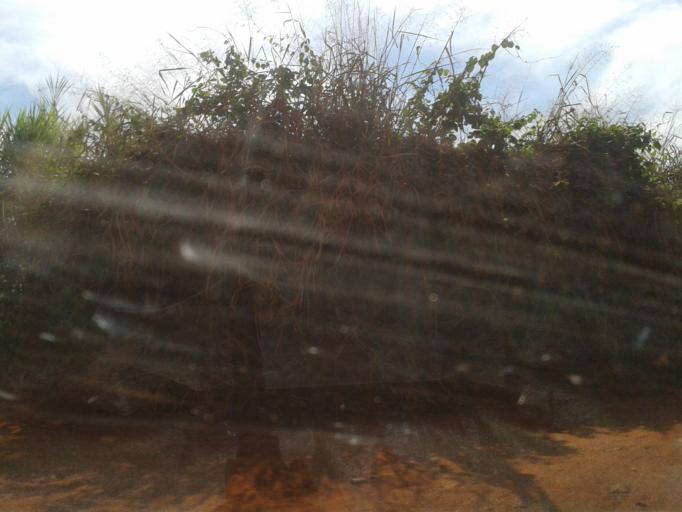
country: BR
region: Goias
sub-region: Goiania
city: Goiania
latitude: -16.6435
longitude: -49.3483
